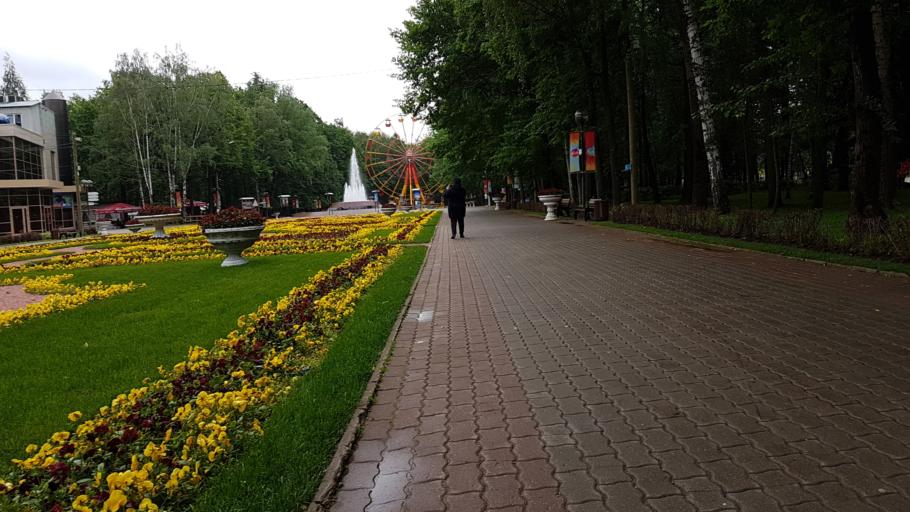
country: RU
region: Moscow
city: Khimki
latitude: 55.8945
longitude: 37.4574
